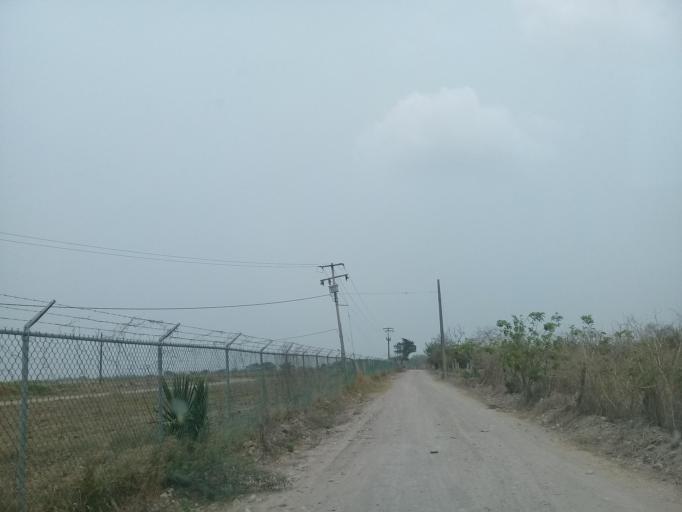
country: MX
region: Veracruz
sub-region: Medellin
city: La Laguna y Monte del Castillo
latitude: 18.9059
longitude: -96.1282
